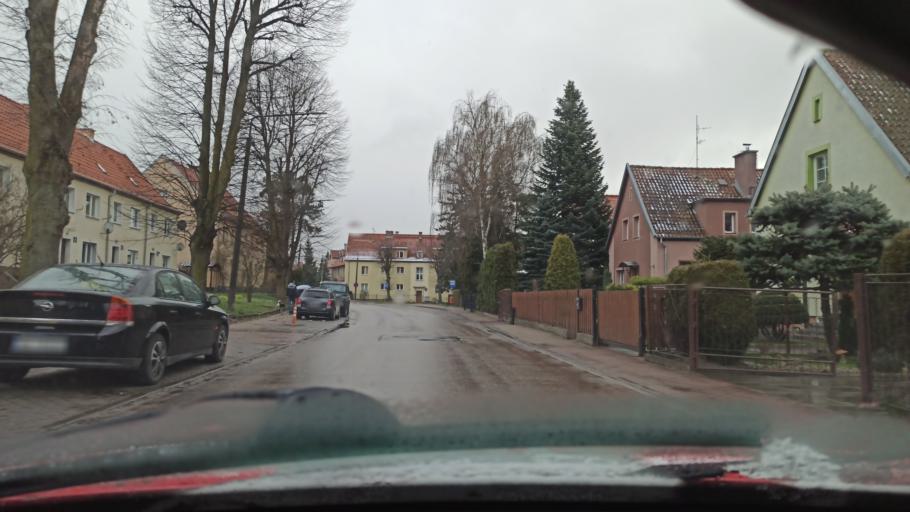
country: PL
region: Warmian-Masurian Voivodeship
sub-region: Powiat elblaski
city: Elblag
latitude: 54.1743
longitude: 19.4126
